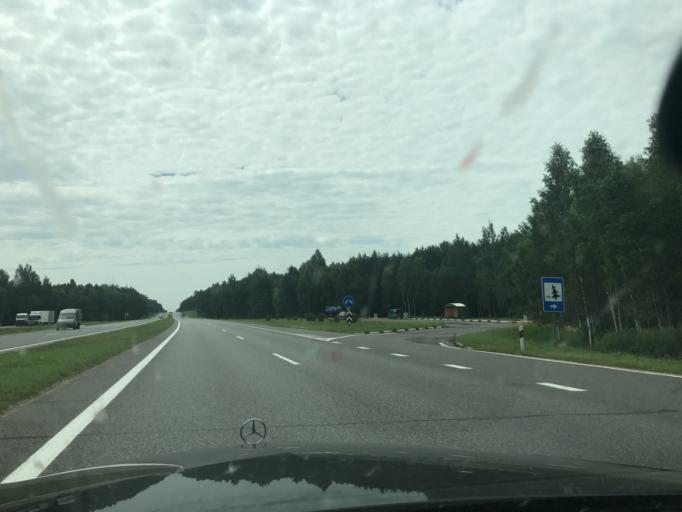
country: BY
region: Minsk
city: Slabada
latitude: 53.9344
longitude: 27.9615
